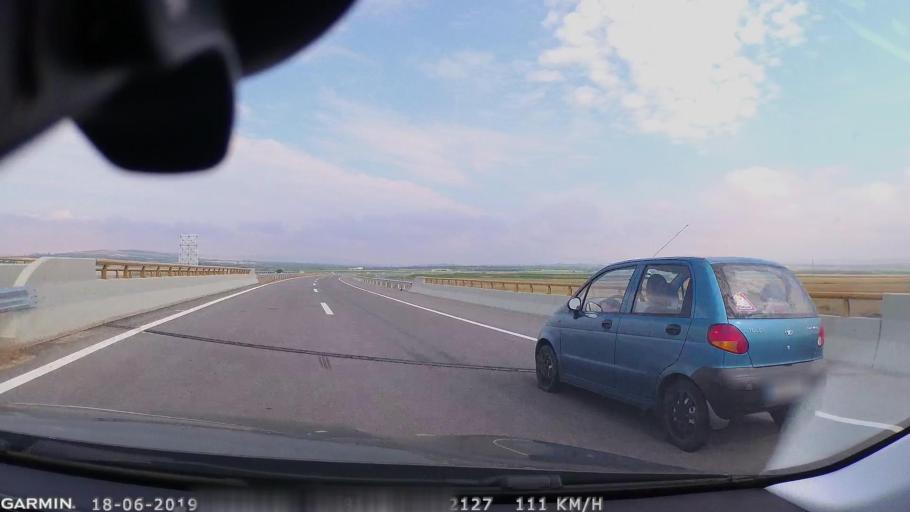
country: MK
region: Sveti Nikole
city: Sveti Nikole
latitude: 41.8149
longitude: 22.0217
